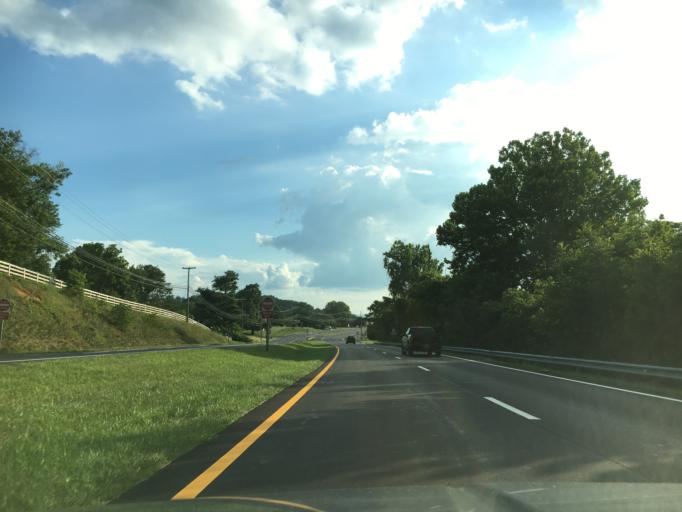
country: US
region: Virginia
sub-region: Roanoke County
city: Vinton
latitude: 37.2825
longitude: -79.8580
